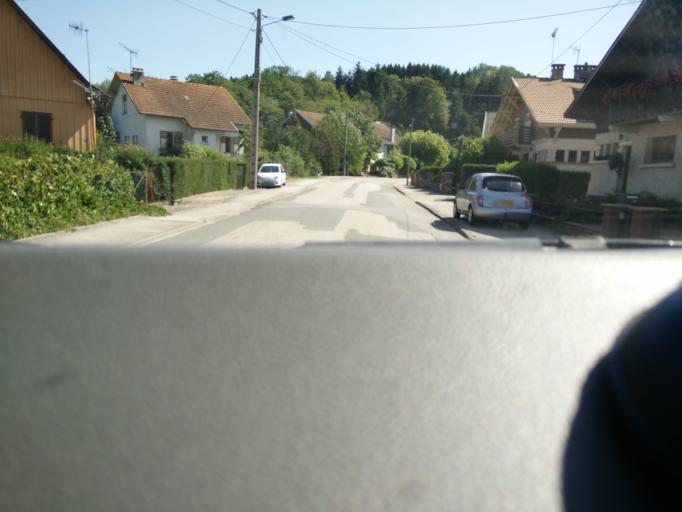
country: FR
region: Lorraine
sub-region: Departement des Vosges
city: Saulcy-sur-Meurthe
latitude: 48.2363
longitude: 6.9623
